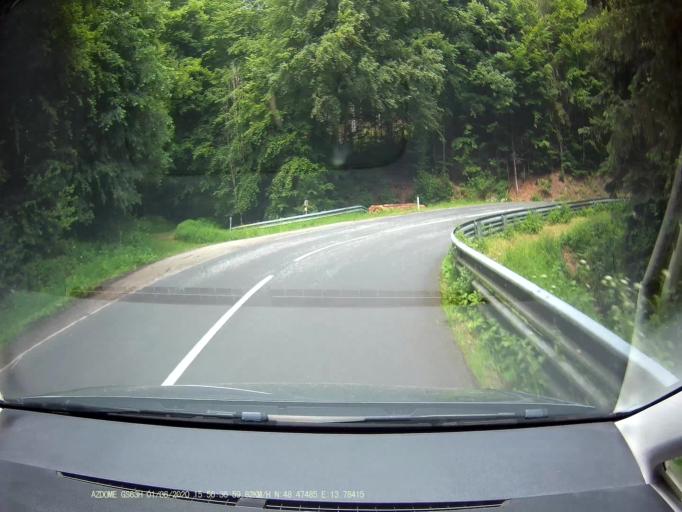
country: AT
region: Upper Austria
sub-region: Politischer Bezirk Rohrbach
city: Pfarrkirchen im Muehlkreis
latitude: 48.4750
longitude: 13.7844
